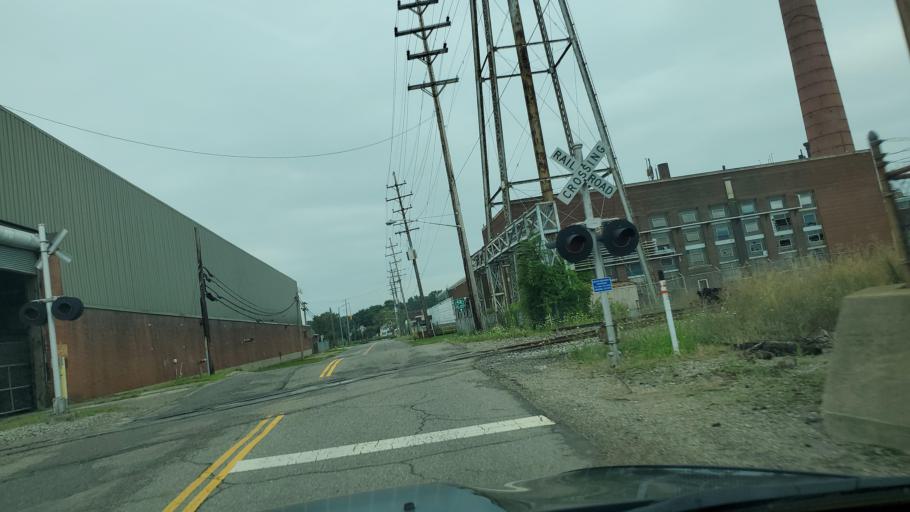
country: US
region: Ohio
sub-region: Trumbull County
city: Warren
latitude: 41.2506
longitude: -80.8107
